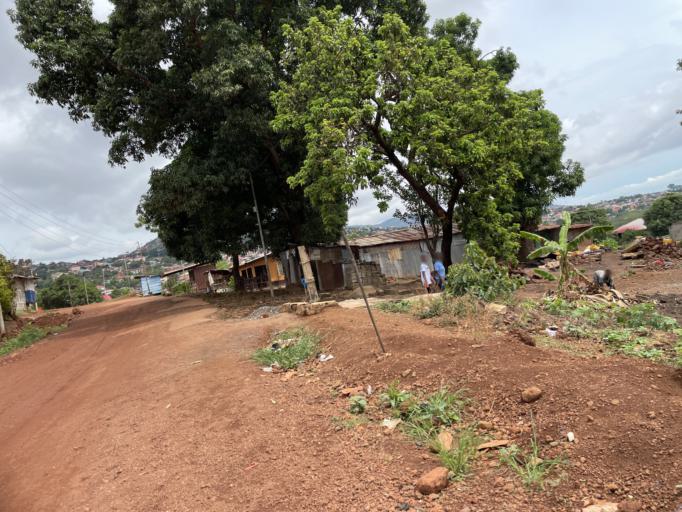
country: SL
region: Western Area
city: Hastings
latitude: 8.4128
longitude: -13.1473
